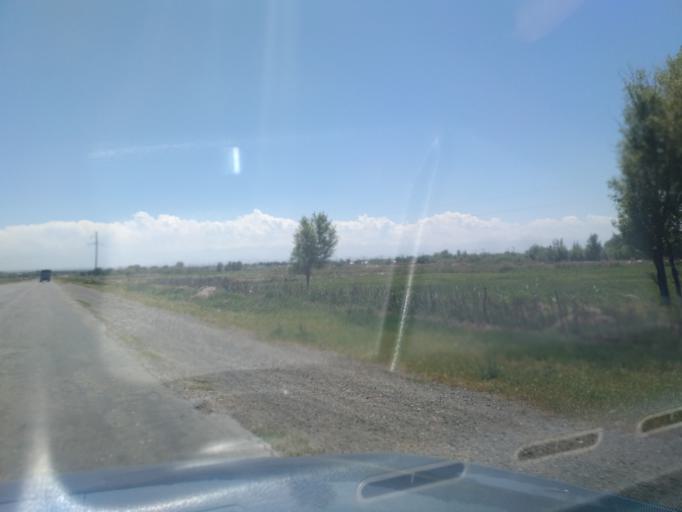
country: TJ
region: Viloyati Sughd
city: Zafarobod
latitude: 40.2287
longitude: 68.8490
